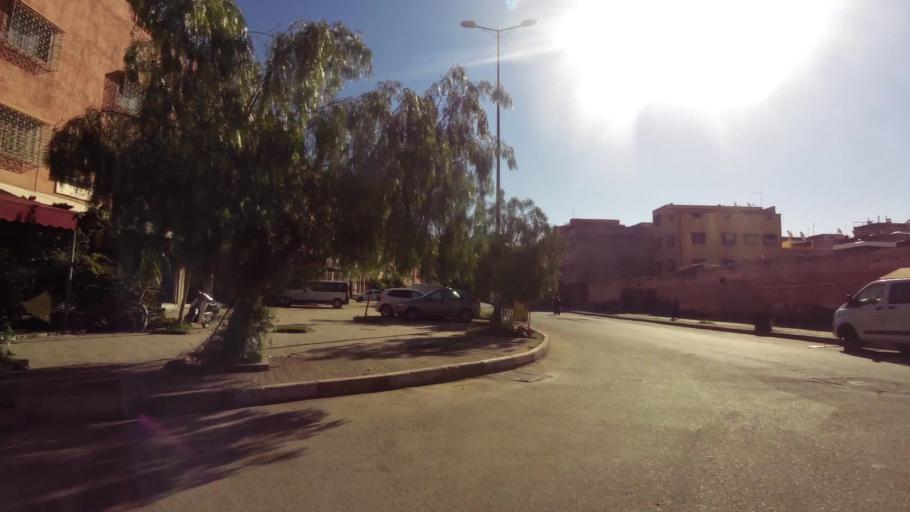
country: MA
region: Marrakech-Tensift-Al Haouz
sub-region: Marrakech
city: Marrakesh
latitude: 31.5965
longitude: -8.0309
